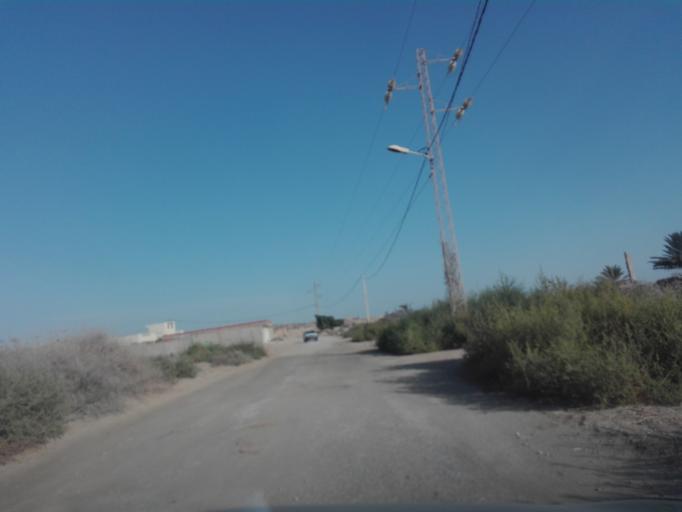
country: TN
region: Qabis
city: Gabes
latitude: 33.9596
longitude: 10.0615
